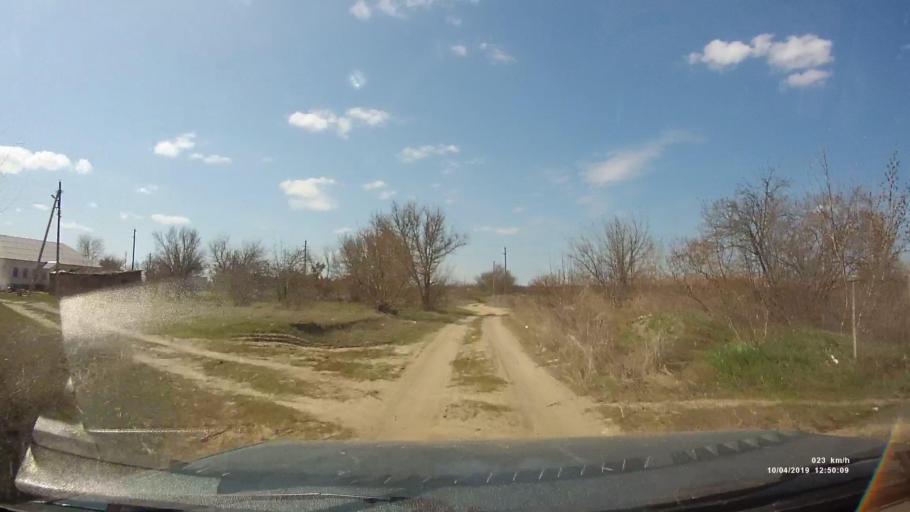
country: RU
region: Rostov
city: Kamensk-Shakhtinskiy
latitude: 48.3582
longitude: 40.2233
